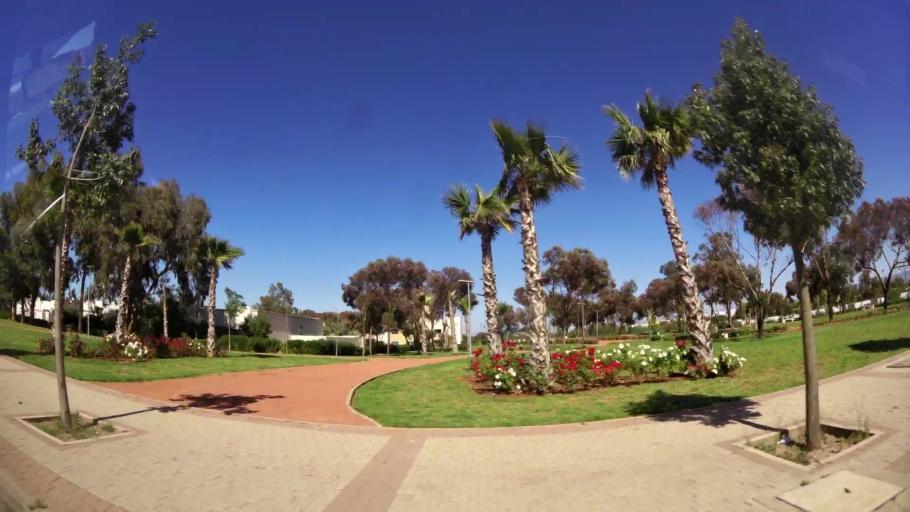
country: MA
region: Oriental
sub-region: Oujda-Angad
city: Oujda
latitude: 34.7164
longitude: -1.9210
